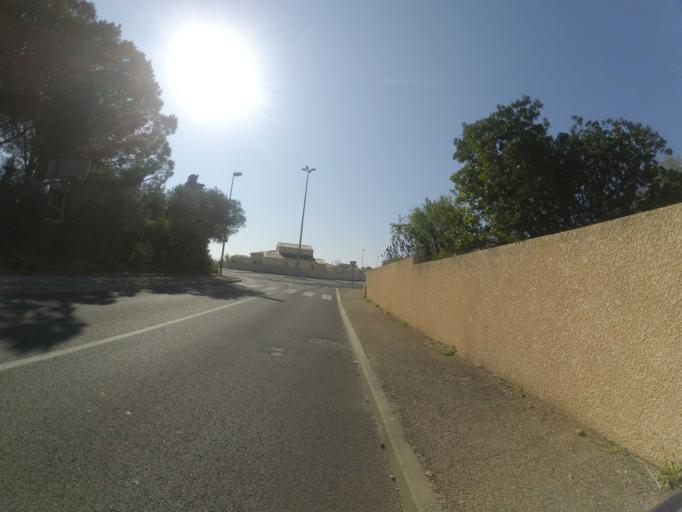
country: FR
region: Languedoc-Roussillon
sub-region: Departement des Pyrenees-Orientales
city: Thuir
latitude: 42.6227
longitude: 2.7510
